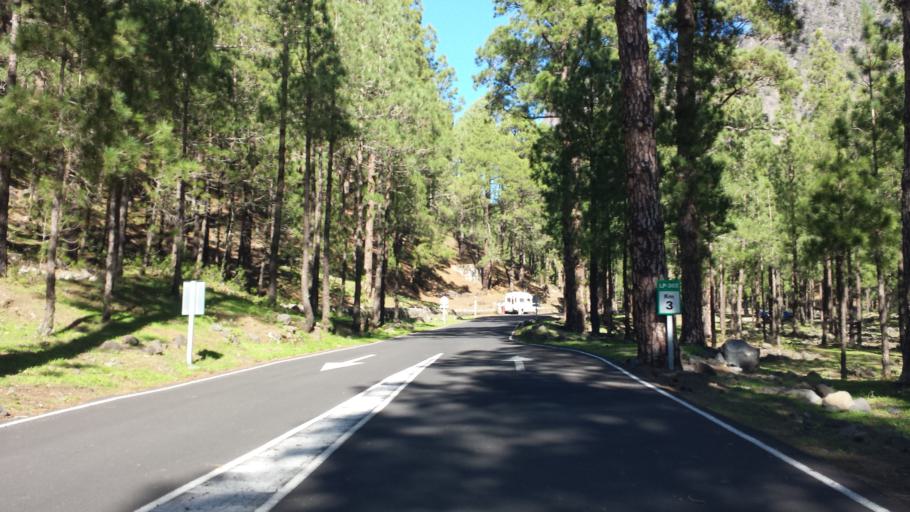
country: ES
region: Canary Islands
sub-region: Provincia de Santa Cruz de Tenerife
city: El Paso
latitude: 28.6780
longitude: -17.8465
